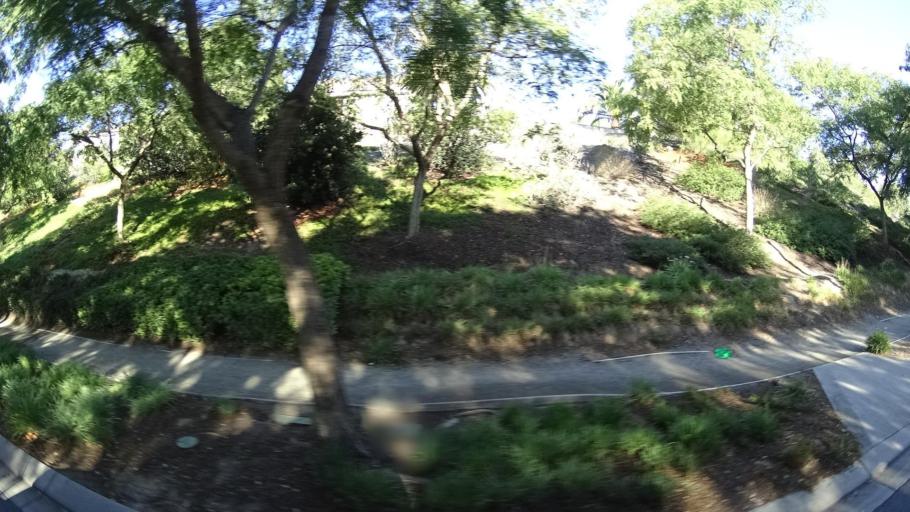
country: US
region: California
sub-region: San Diego County
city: La Presa
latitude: 32.6514
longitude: -116.9408
